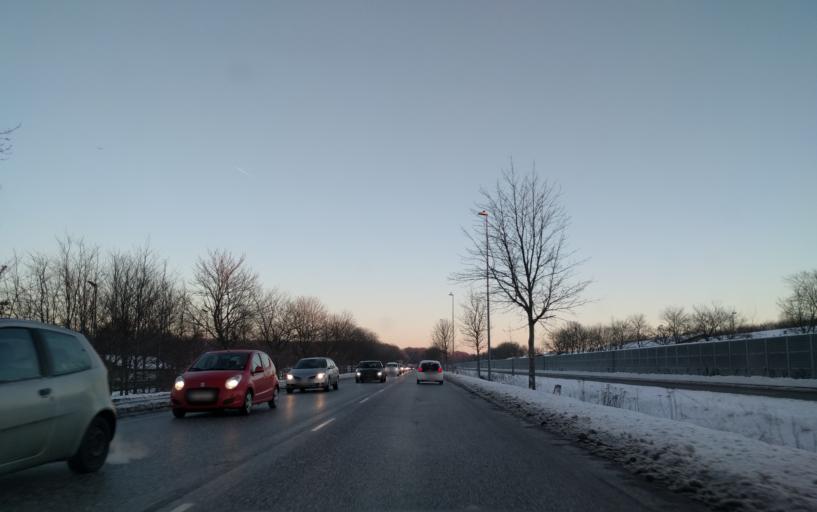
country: DK
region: North Denmark
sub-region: Alborg Kommune
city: Aalborg
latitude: 57.0235
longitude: 9.9451
